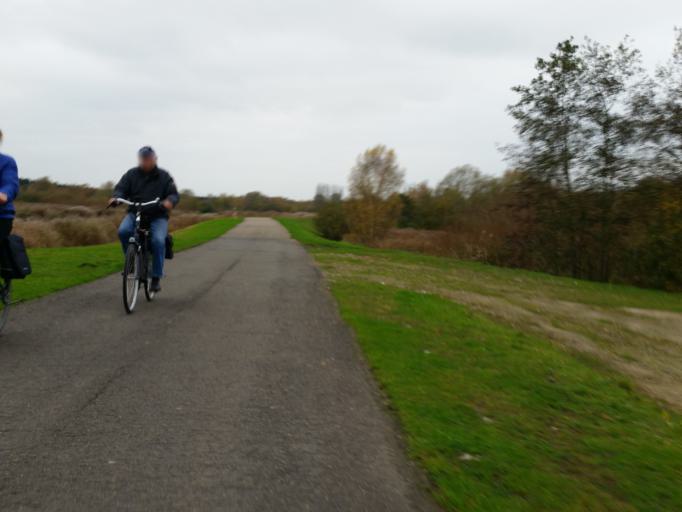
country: BE
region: Flanders
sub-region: Provincie Antwerpen
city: Lier
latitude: 51.1148
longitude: 4.5435
